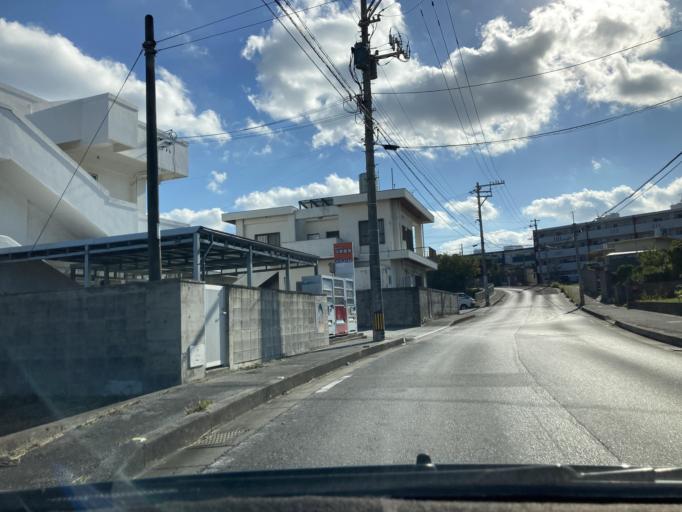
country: JP
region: Okinawa
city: Katsuren-haebaru
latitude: 26.3127
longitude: 127.9105
